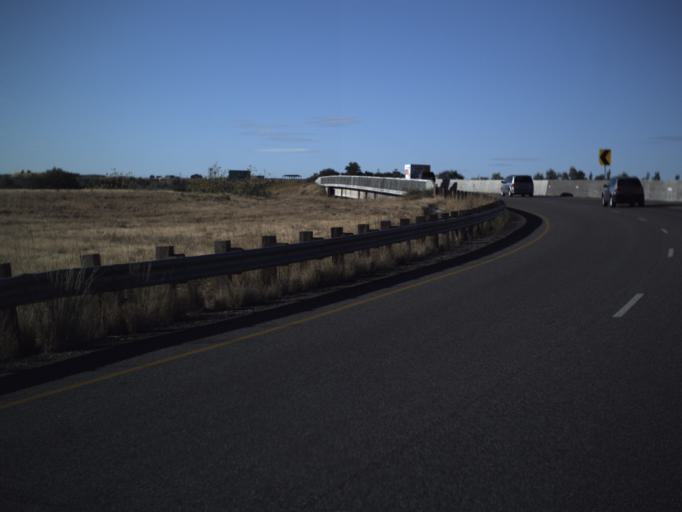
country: US
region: Utah
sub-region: Weber County
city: Riverdale
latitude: 41.1866
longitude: -112.0107
